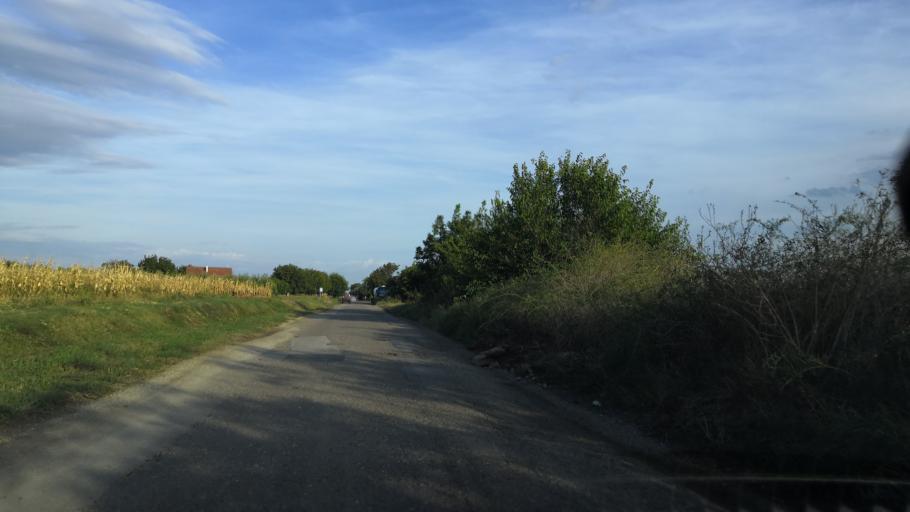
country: RS
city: Novi Slankamen
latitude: 45.1360
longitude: 20.2380
